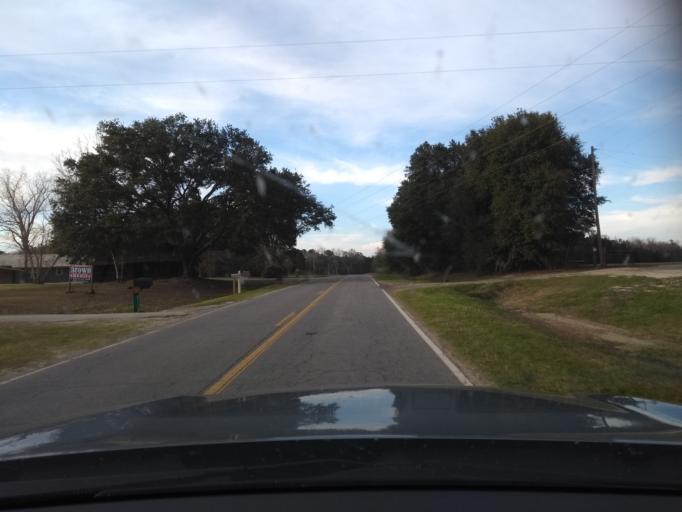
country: US
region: Georgia
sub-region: Evans County
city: Claxton
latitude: 32.2127
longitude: -81.7682
